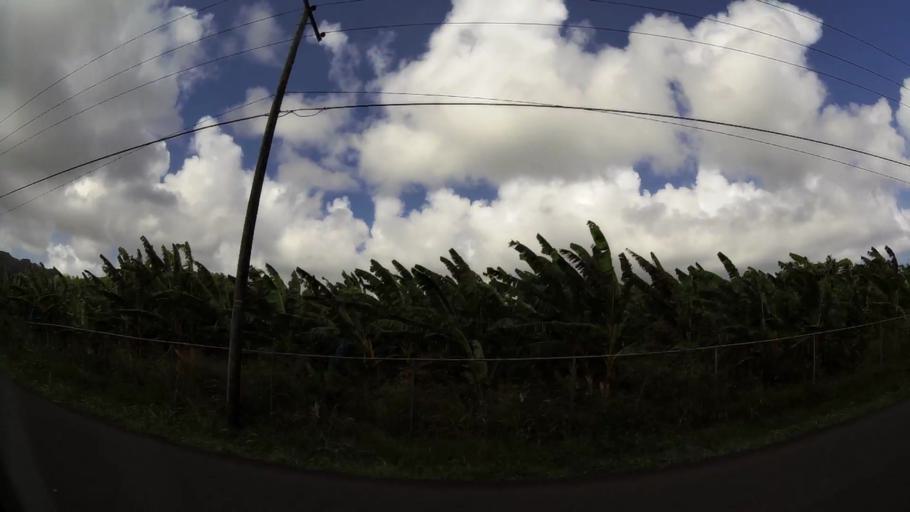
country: LC
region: Dennery Quarter
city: Dennery
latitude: 13.9330
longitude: -60.9267
